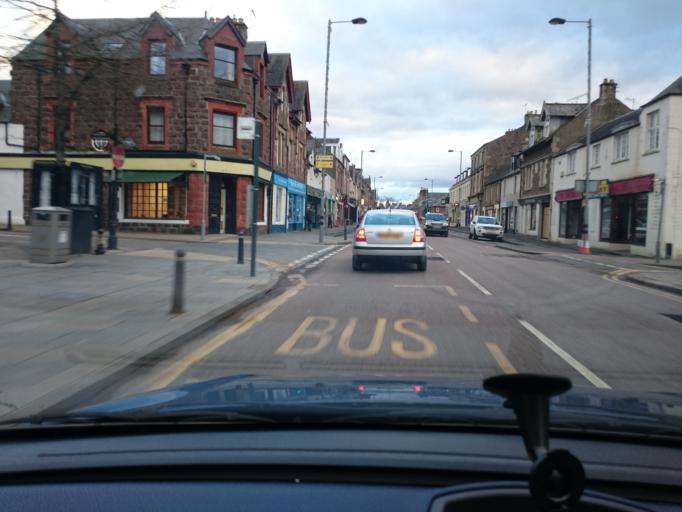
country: GB
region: Scotland
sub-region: Stirling
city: Callander
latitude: 56.2437
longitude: -4.2147
